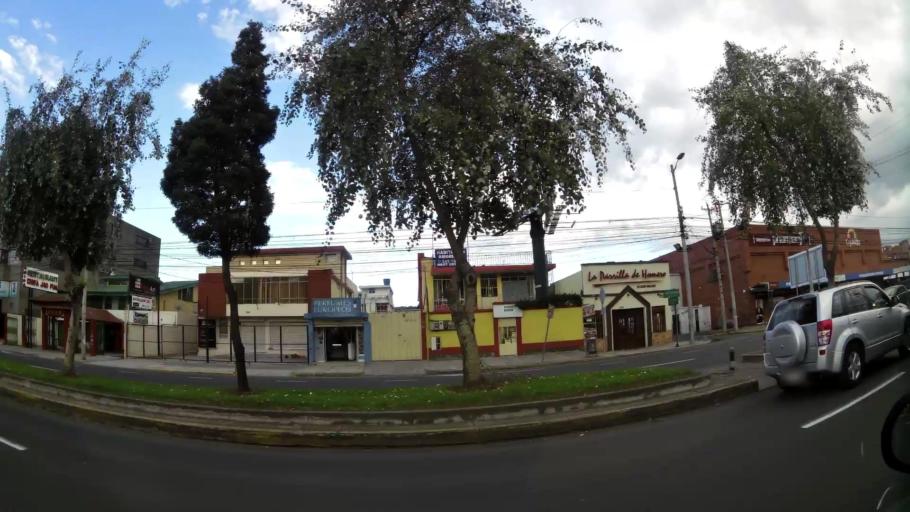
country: EC
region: Pichincha
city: Quito
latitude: -0.1679
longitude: -78.4842
